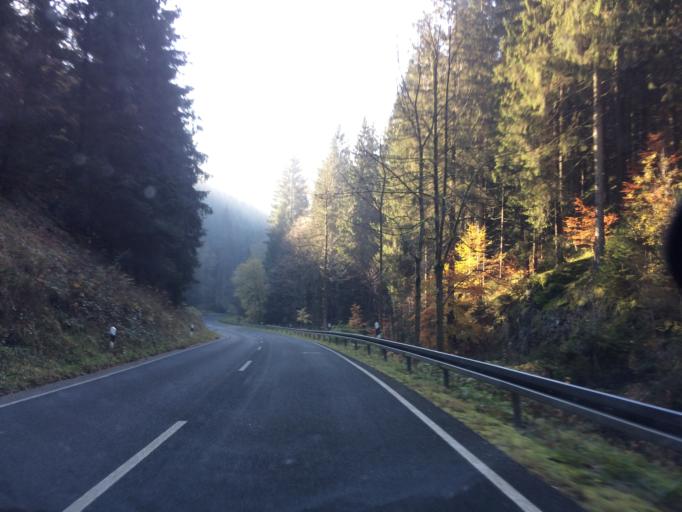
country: DE
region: Lower Saxony
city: Sankt Andreasberg
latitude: 51.7001
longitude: 10.5122
